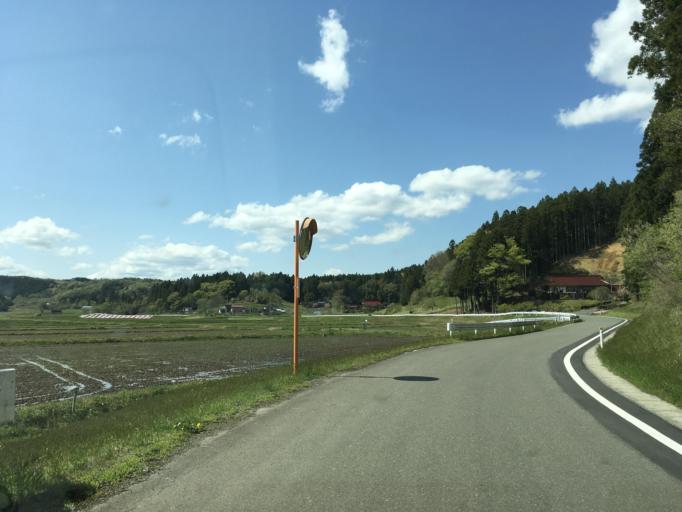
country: JP
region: Iwate
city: Ichinoseki
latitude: 38.8359
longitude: 141.2471
